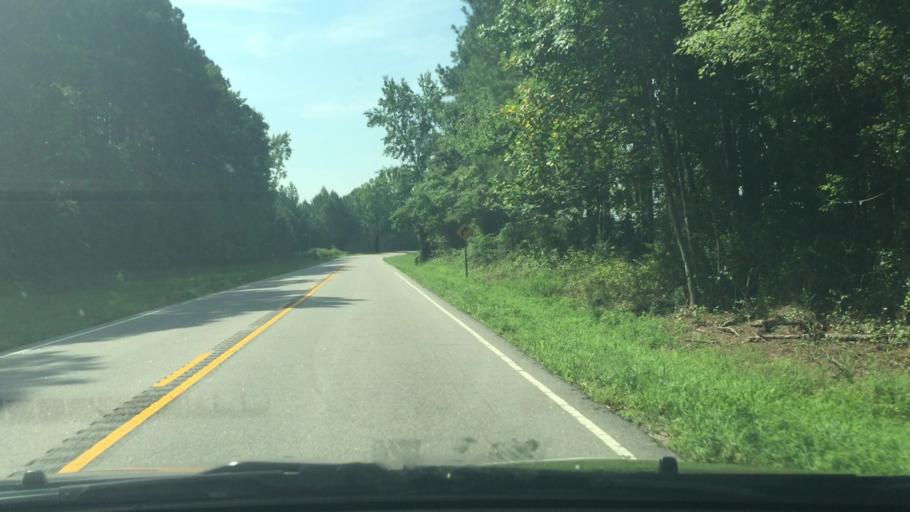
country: US
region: Virginia
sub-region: Southampton County
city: Courtland
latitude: 36.8229
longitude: -77.1254
